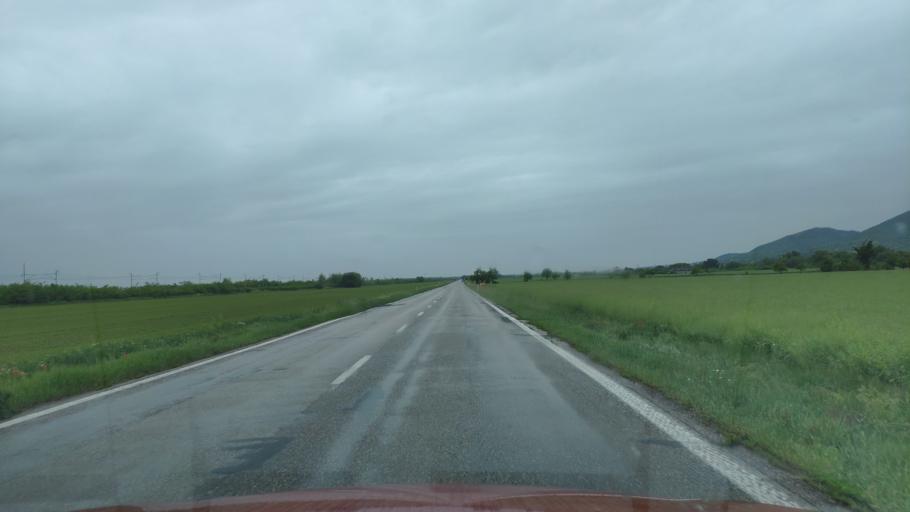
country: HU
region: Borsod-Abauj-Zemplen
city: Satoraljaujhely
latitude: 48.4394
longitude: 21.6554
